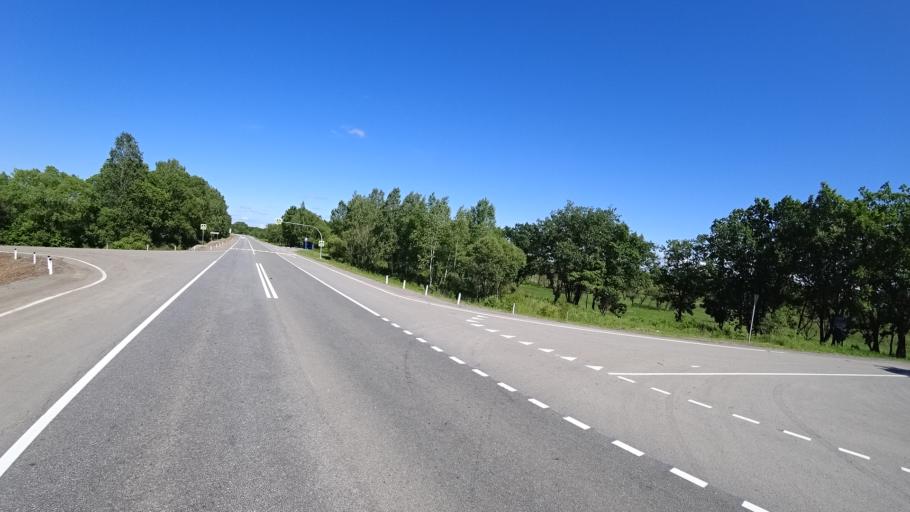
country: RU
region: Khabarovsk Krai
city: Khor
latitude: 47.8964
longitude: 135.0264
